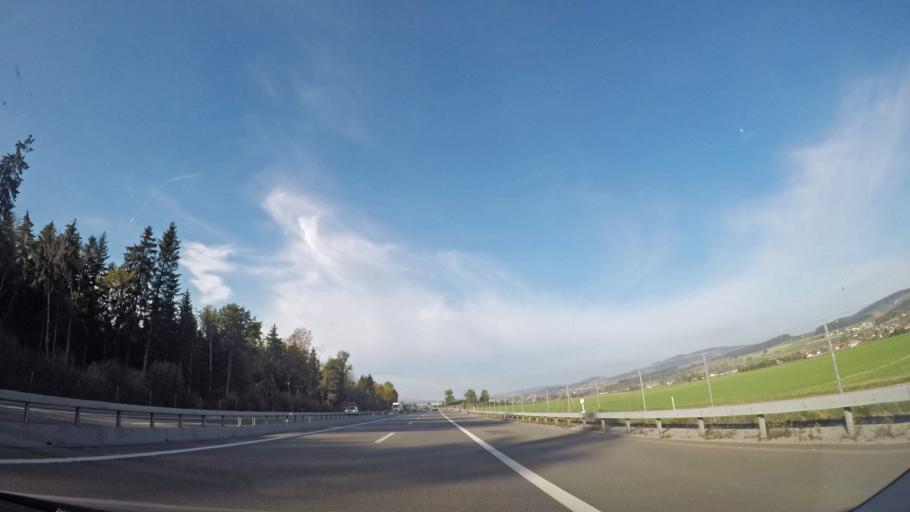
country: CH
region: Bern
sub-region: Bern-Mittelland District
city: Niederwichtrach
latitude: 46.8431
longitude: 7.5596
